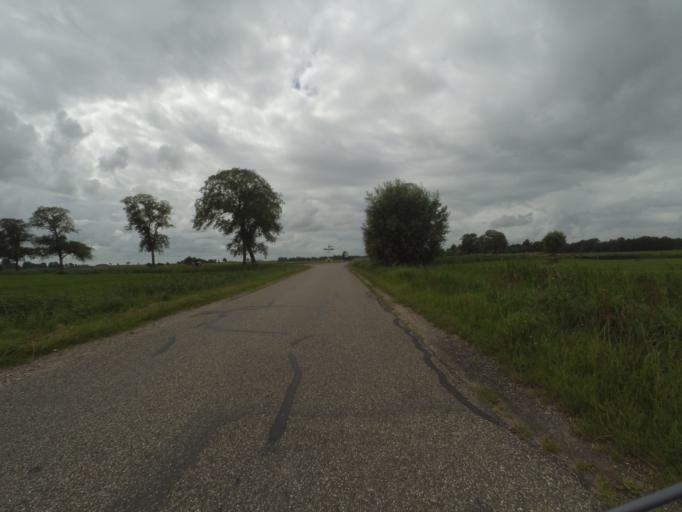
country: NL
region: Friesland
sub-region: Gemeente Kollumerland en Nieuwkruisland
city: Kollumerzwaag
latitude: 53.2989
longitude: 6.0835
